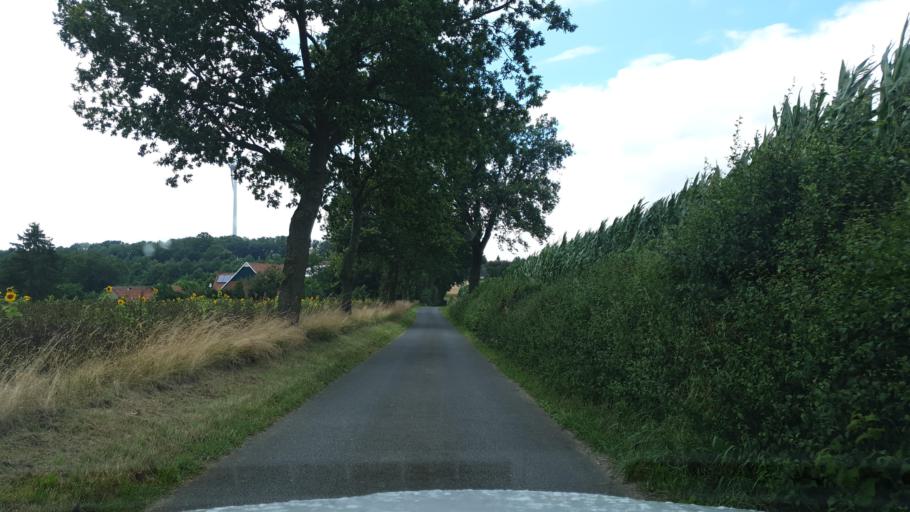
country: DE
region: North Rhine-Westphalia
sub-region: Regierungsbezirk Detmold
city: Bad Salzuflen
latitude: 52.1305
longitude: 8.7445
